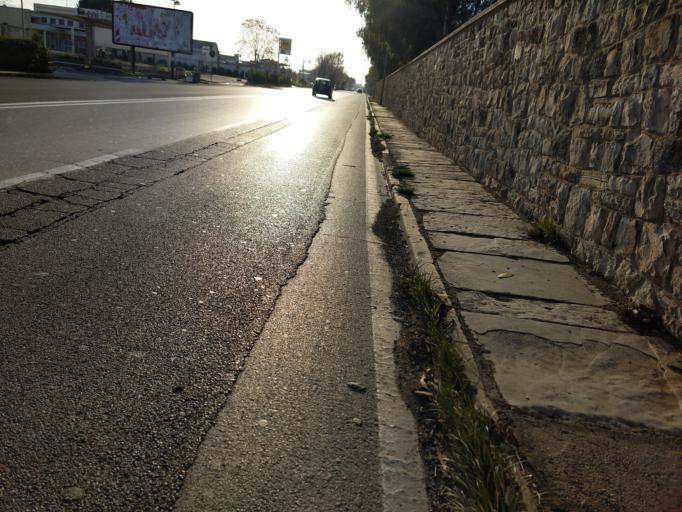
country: IT
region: Apulia
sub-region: Provincia di Bari
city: Bari
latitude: 41.1145
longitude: 16.8334
